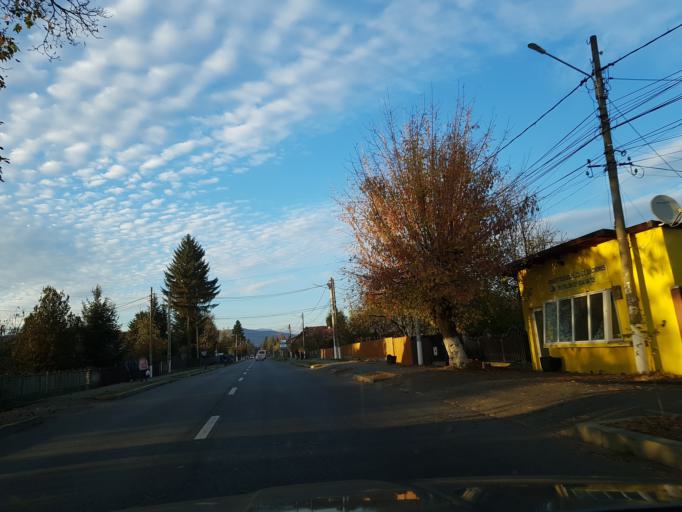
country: RO
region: Prahova
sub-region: Oras Breaza
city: Breaza
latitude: 45.1873
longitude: 25.6618
